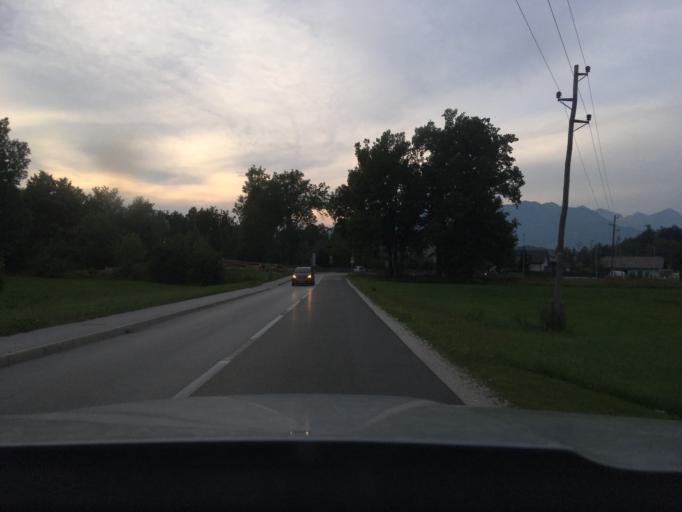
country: SI
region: Kamnik
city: Smarca
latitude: 46.1971
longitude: 14.6011
